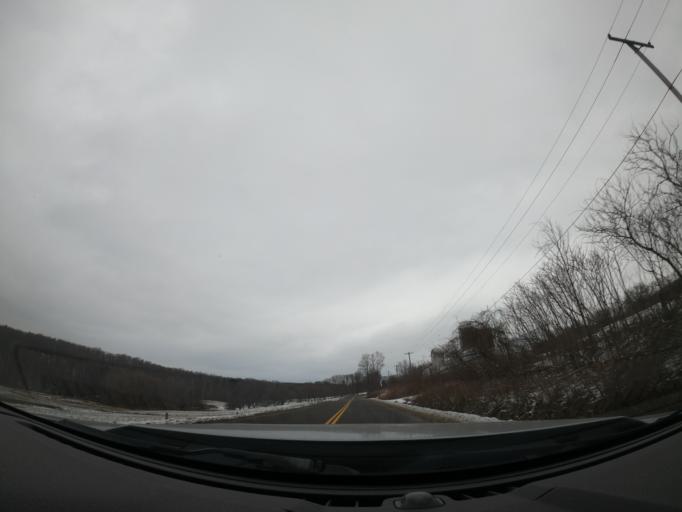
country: US
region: New York
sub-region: Cayuga County
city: Moravia
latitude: 42.7447
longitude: -76.3796
